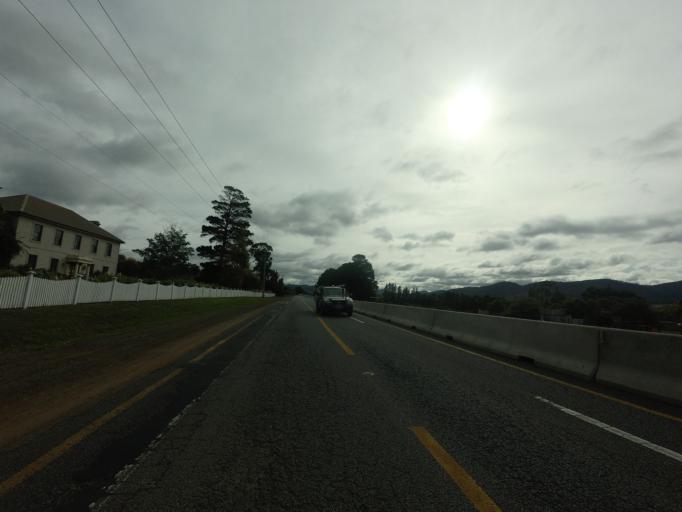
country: AU
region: Tasmania
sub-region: Brighton
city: Bridgewater
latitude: -42.6715
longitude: 147.2573
